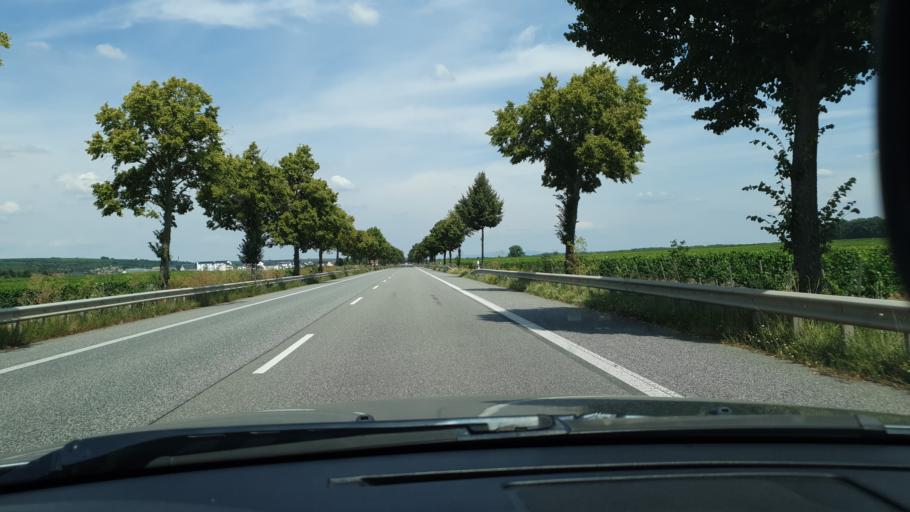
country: DE
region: Rheinland-Pfalz
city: Alsheim
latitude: 49.7596
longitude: 8.3523
